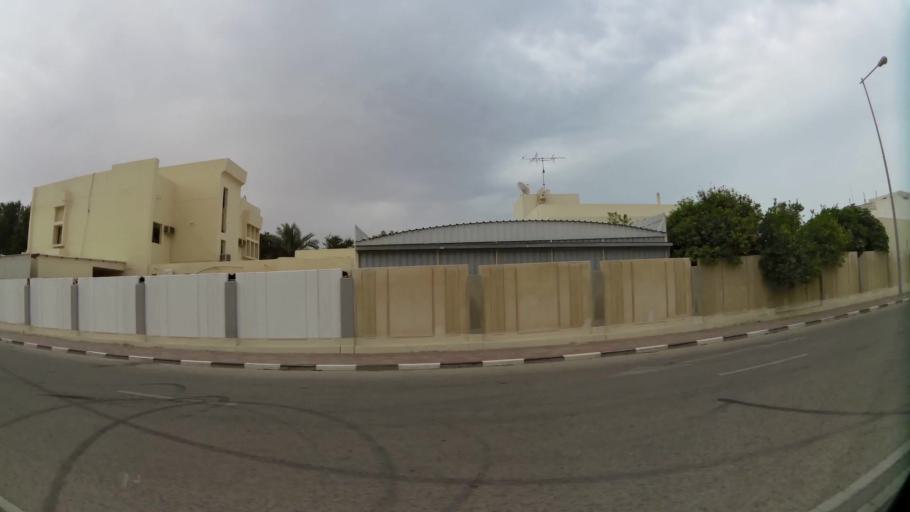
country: QA
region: Baladiyat ad Dawhah
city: Doha
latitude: 25.3324
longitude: 51.5069
